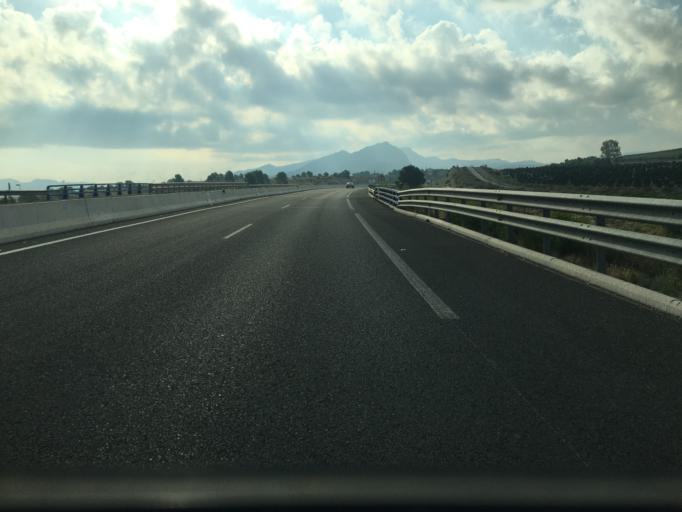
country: ES
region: Murcia
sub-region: Murcia
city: Beniel
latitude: 37.9968
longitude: -0.9860
